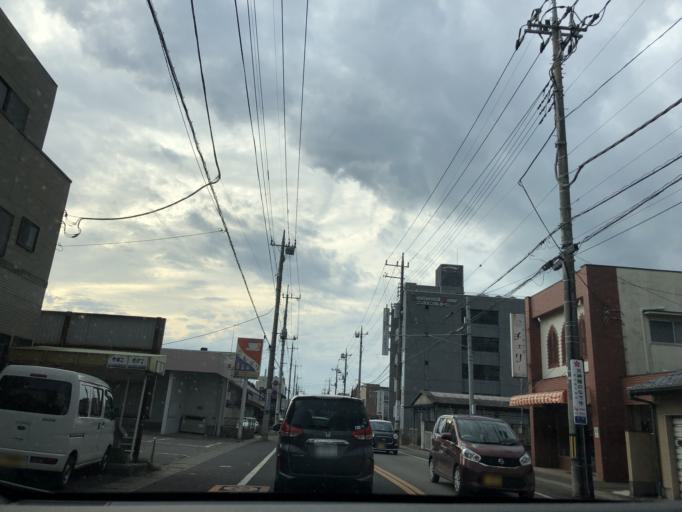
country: JP
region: Tochigi
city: Sano
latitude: 36.3136
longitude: 139.5733
